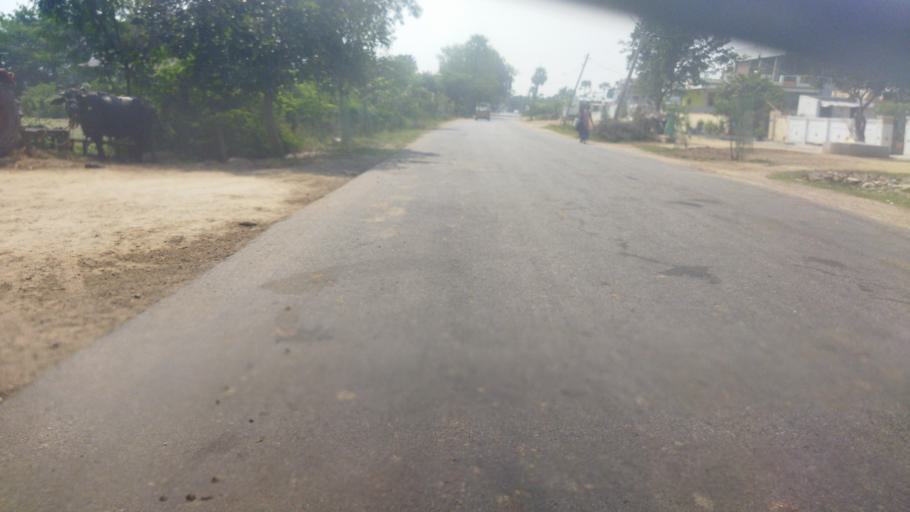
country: IN
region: Telangana
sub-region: Nalgonda
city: Nalgonda
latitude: 17.1502
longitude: 79.3104
